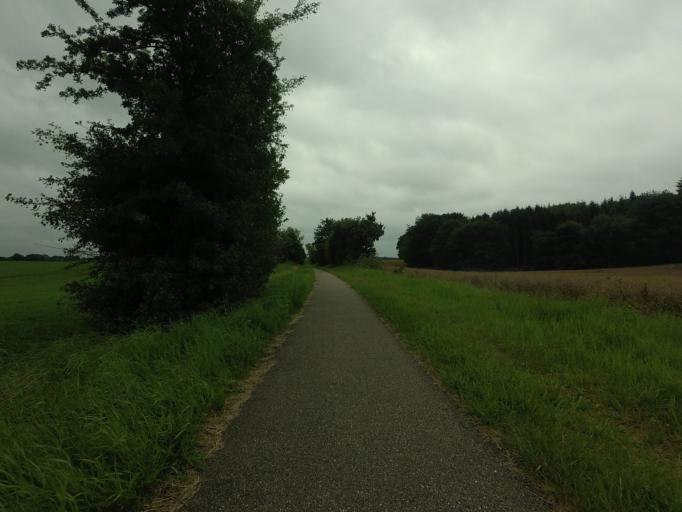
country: DK
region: Central Jutland
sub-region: Horsens Kommune
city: Braedstrup
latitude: 55.9922
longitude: 9.5890
